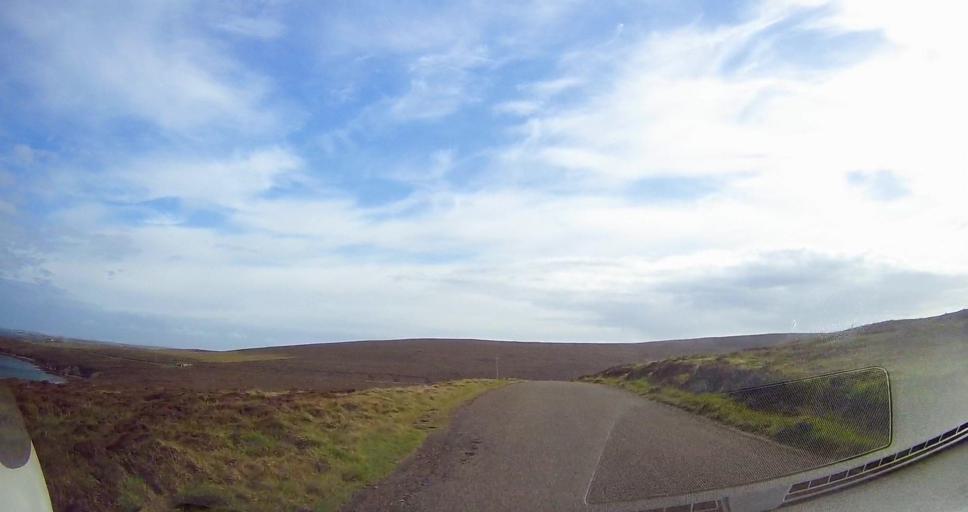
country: GB
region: Scotland
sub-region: Orkney Islands
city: Stromness
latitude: 58.8655
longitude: -3.2201
